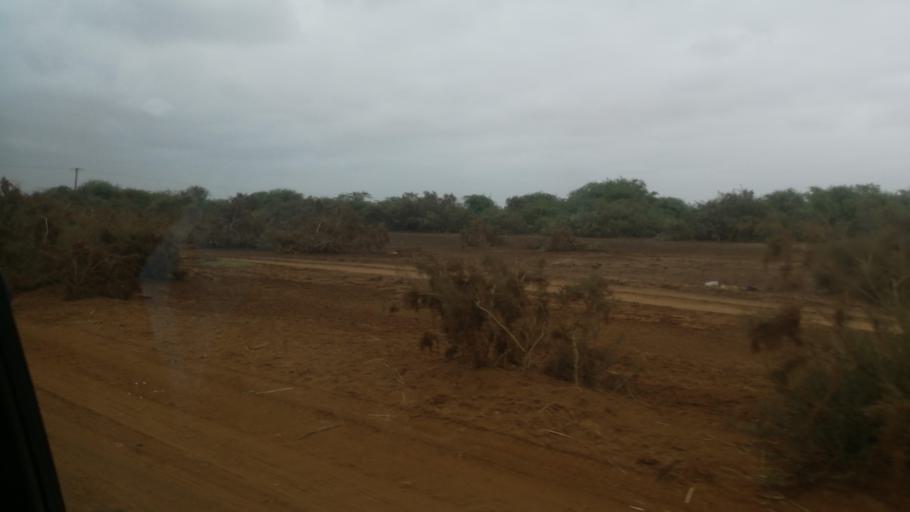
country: SN
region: Saint-Louis
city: Rosso
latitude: 16.2796
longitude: -16.1651
